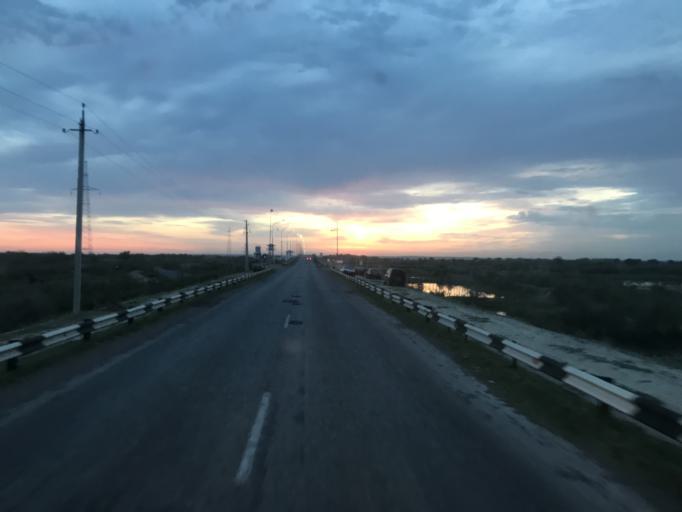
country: KZ
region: Ongtustik Qazaqstan
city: Ilyich
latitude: 41.0268
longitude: 68.5127
